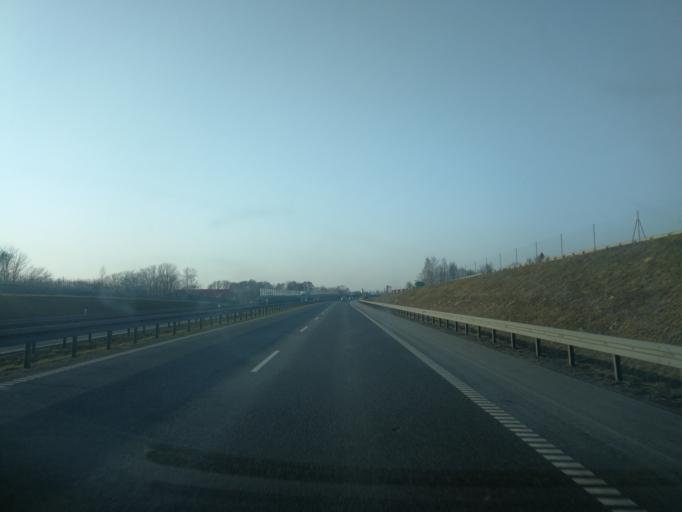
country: PL
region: Warmian-Masurian Voivodeship
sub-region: Powiat elblaski
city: Gronowo Gorne
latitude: 54.1214
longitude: 19.4681
